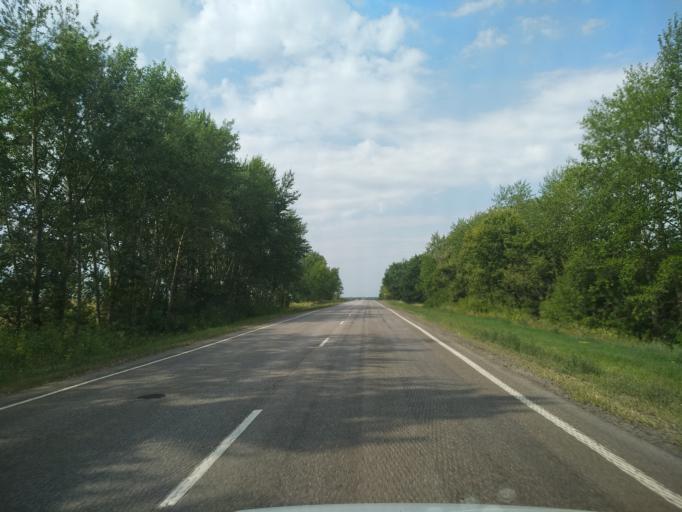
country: RU
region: Voronezj
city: Verkhnyaya Khava
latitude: 51.6951
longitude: 39.9515
